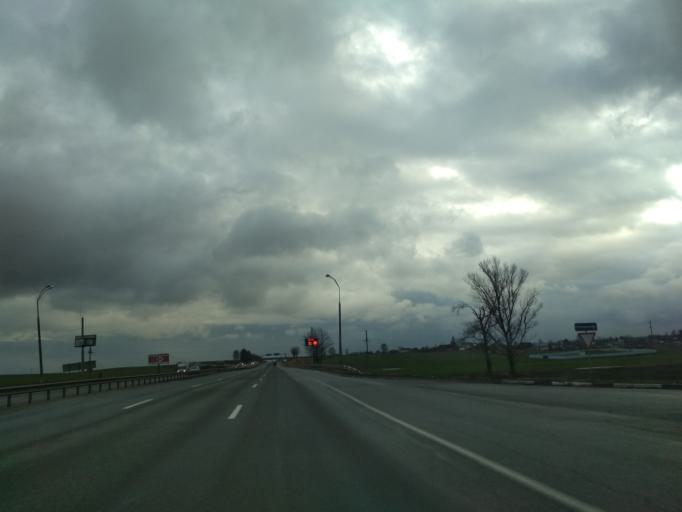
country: BY
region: Minsk
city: Pryvol'ny
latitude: 53.7974
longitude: 27.8084
